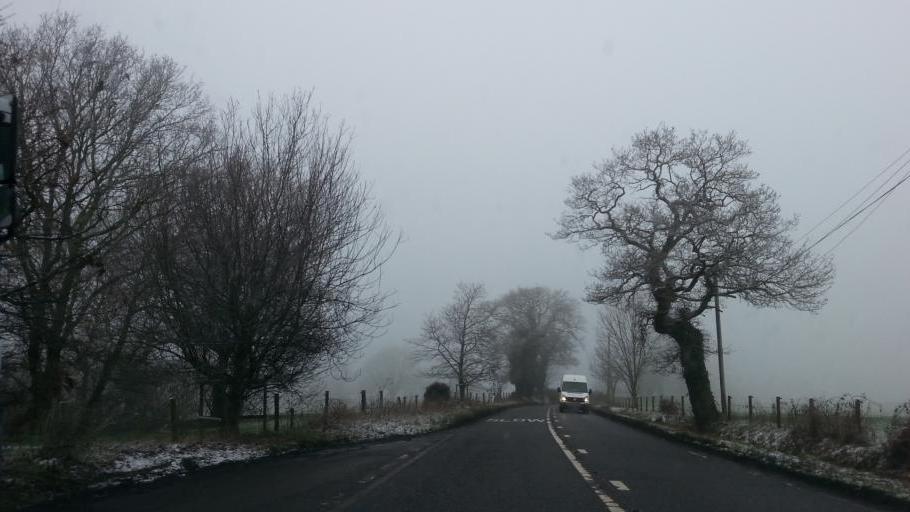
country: GB
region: England
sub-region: Cheshire East
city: Eaton
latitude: 53.1992
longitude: -2.2241
